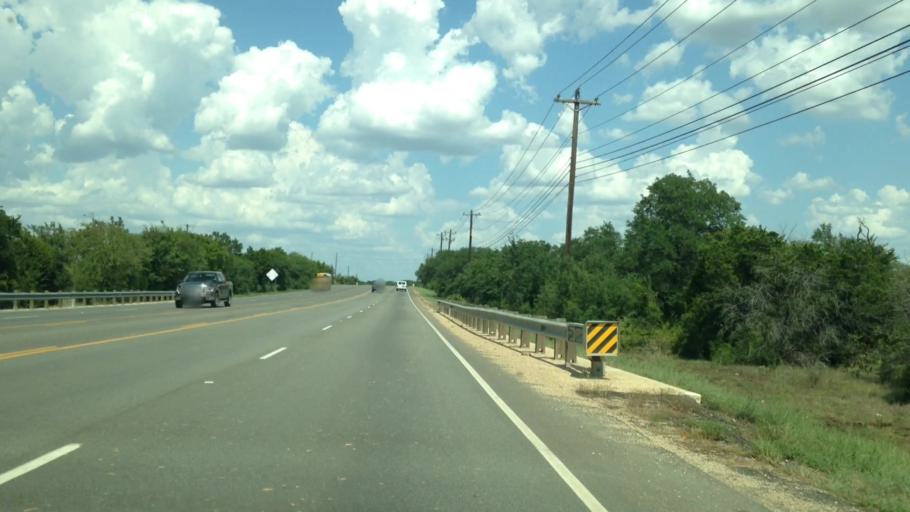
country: US
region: Texas
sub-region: Williamson County
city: Georgetown
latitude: 30.6329
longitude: -97.7349
